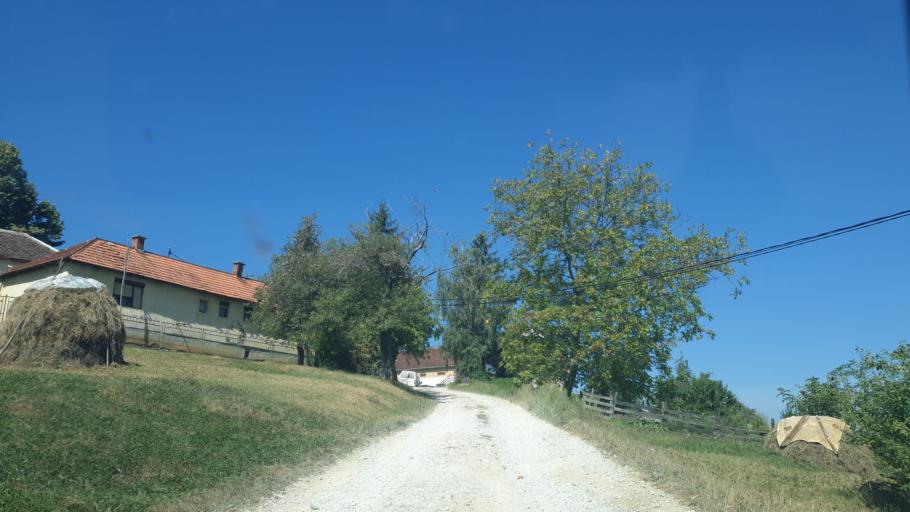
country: RS
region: Central Serbia
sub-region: Kolubarski Okrug
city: Mionica
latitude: 44.1982
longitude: 20.0223
